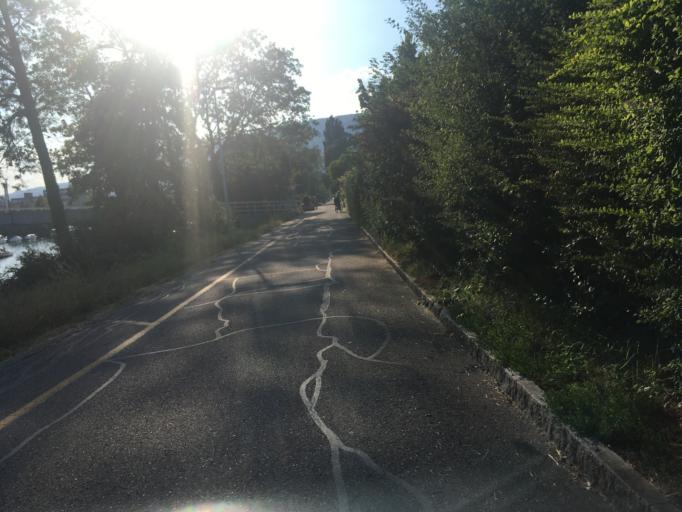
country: CH
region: Bern
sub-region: Biel/Bienne District
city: Bellmund
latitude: 47.1201
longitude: 7.2535
